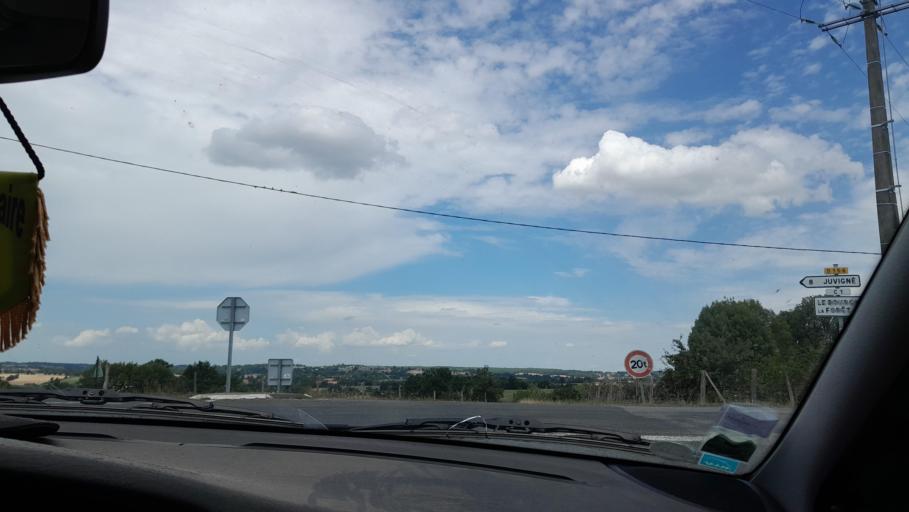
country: FR
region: Pays de la Loire
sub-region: Departement de la Mayenne
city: Juvigne
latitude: 48.1714
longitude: -1.0398
